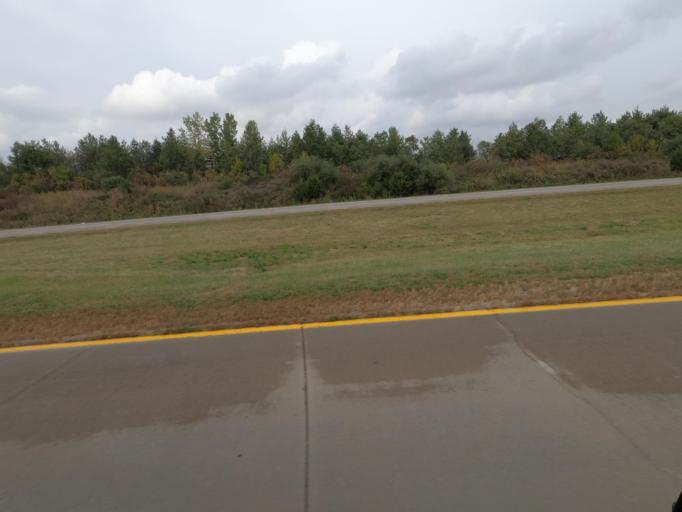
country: US
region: Iowa
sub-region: Wapello County
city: Ottumwa
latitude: 41.0963
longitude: -92.4691
